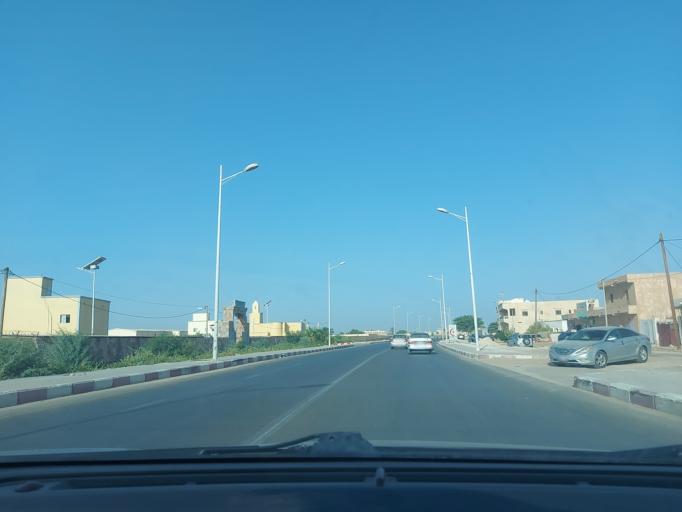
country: MR
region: Nouakchott
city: Nouakchott
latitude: 18.0844
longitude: -15.9937
